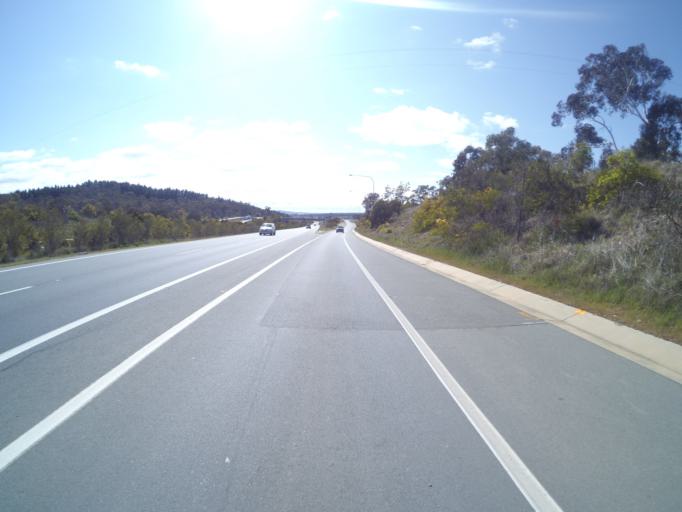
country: AU
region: Australian Capital Territory
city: Kaleen
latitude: -35.2036
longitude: 149.2071
